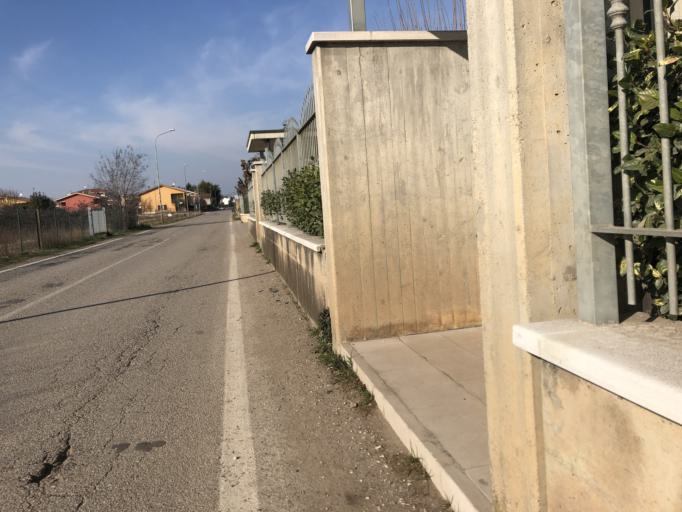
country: IT
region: Veneto
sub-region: Provincia di Verona
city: Lugagnano
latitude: 45.4293
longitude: 10.8814
